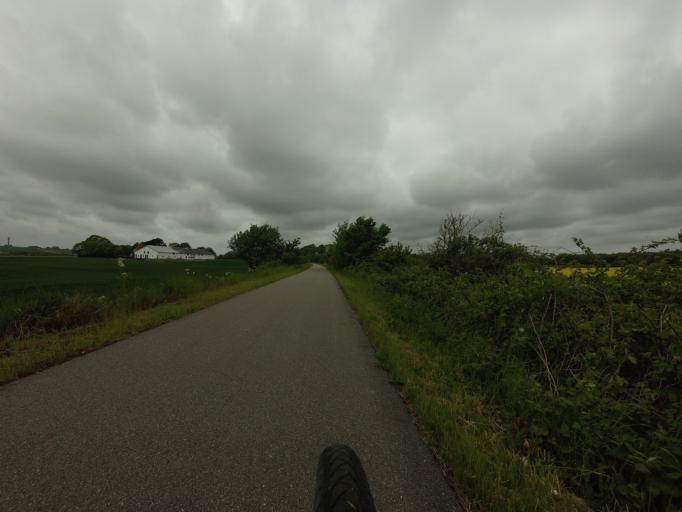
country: DK
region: Zealand
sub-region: Slagelse Kommune
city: Slagelse
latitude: 55.3724
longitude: 11.3816
